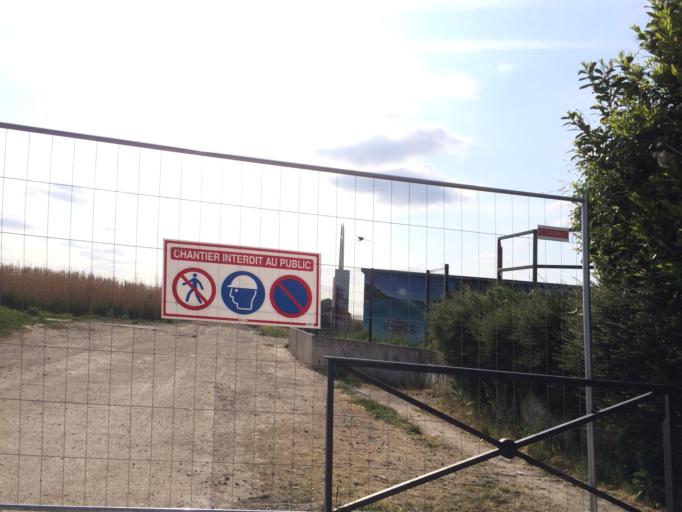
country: FR
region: Ile-de-France
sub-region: Departement de l'Essonne
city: Paray-Vieille-Poste
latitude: 48.7149
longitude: 2.3562
